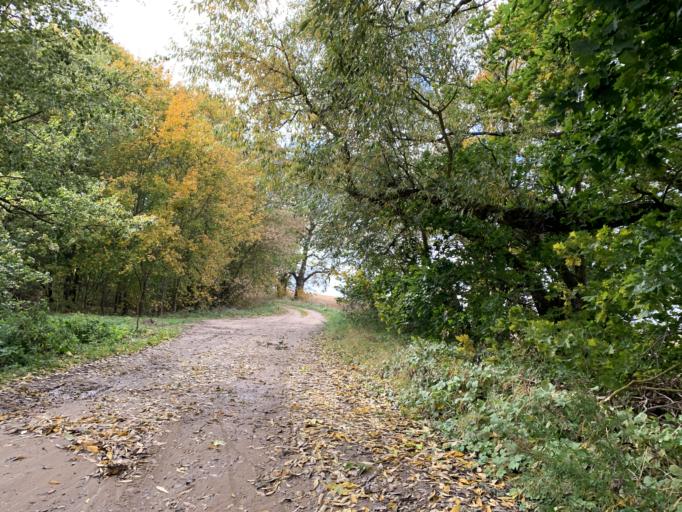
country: BY
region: Minsk
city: Nyasvizh
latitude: 53.2349
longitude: 26.7060
